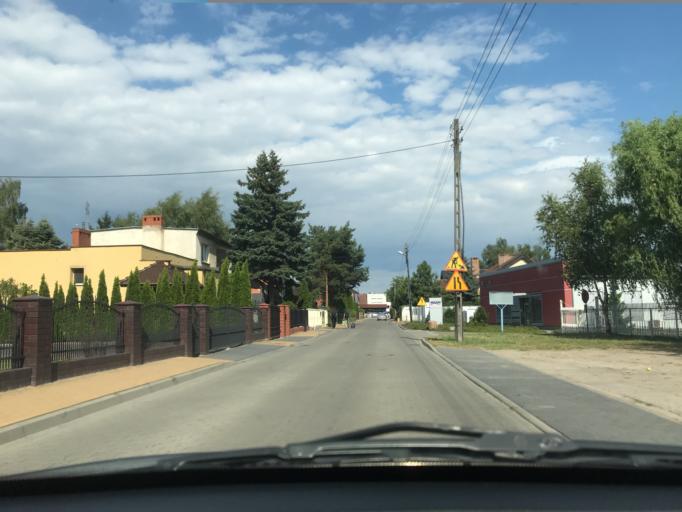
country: PL
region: Greater Poland Voivodeship
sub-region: Powiat poznanski
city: Plewiska
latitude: 52.3724
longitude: 16.8213
